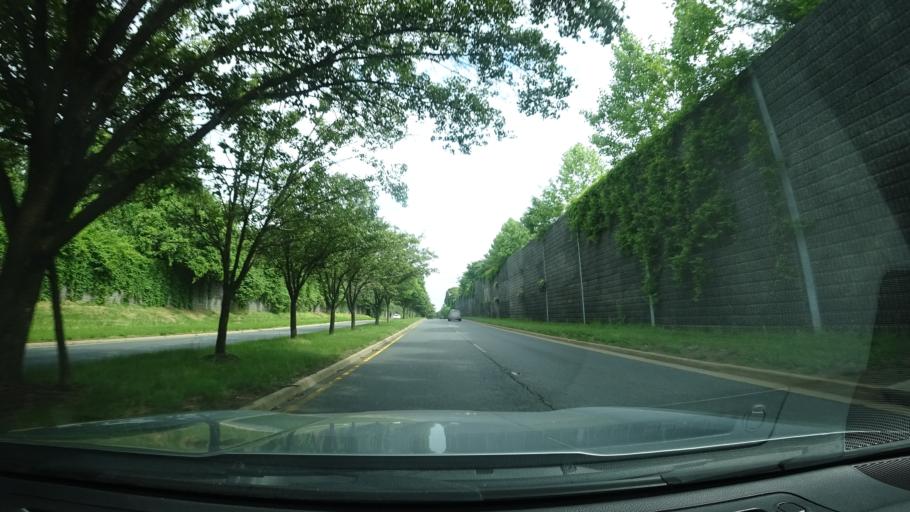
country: US
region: Virginia
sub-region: Fairfax County
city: Dranesville
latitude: 39.0151
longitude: -77.3624
